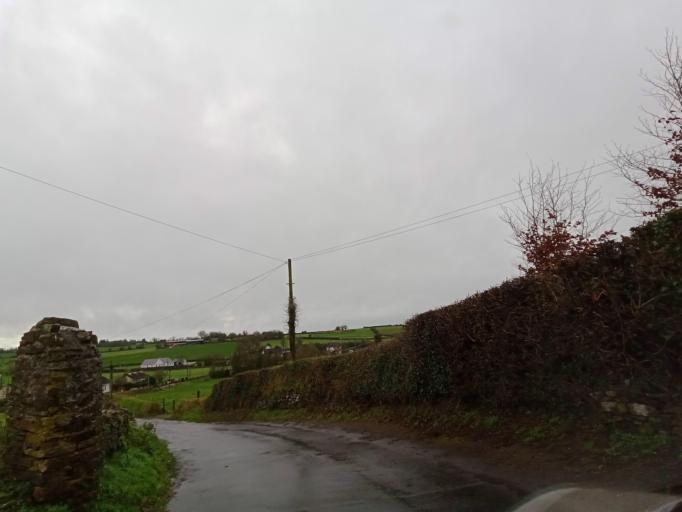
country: IE
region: Munster
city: Fethard
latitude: 52.5650
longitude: -7.6804
